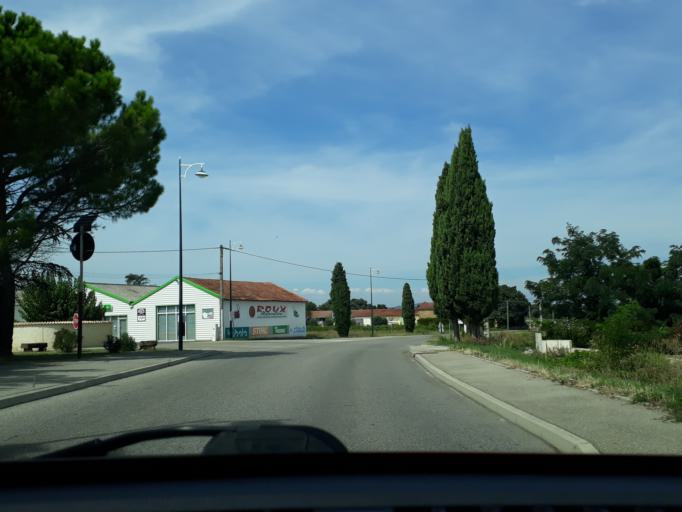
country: FR
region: Rhone-Alpes
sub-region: Departement de la Drome
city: Rochegude
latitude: 44.2524
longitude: 4.8261
